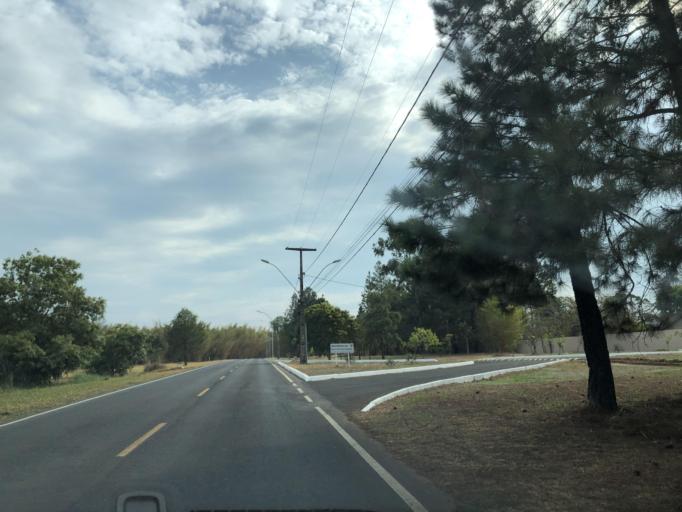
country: BR
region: Federal District
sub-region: Brasilia
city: Brasilia
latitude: -15.9425
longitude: -47.9806
